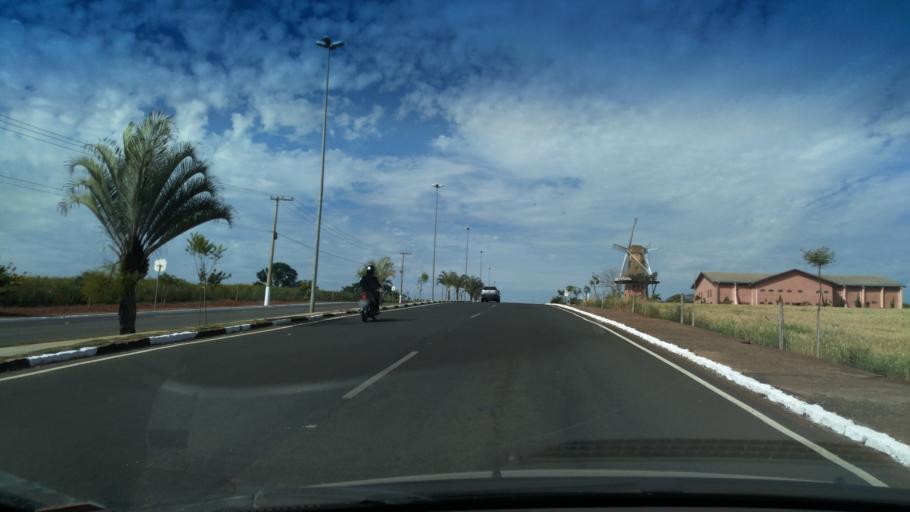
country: BR
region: Sao Paulo
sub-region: Jaguariuna
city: Jaguariuna
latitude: -22.6233
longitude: -47.0627
